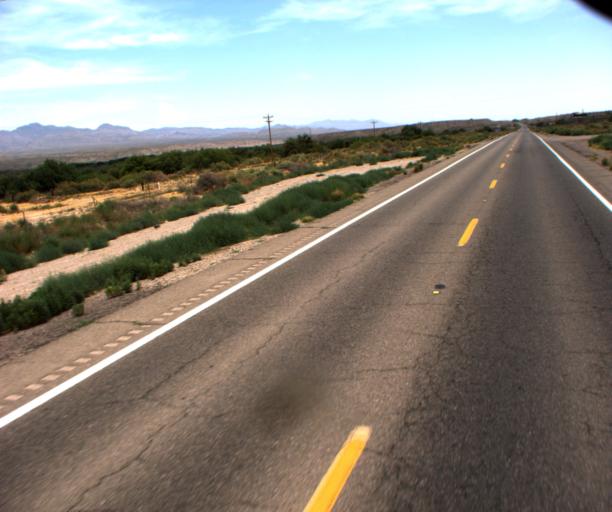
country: US
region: Arizona
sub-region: Graham County
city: Bylas
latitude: 33.0894
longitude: -110.0622
